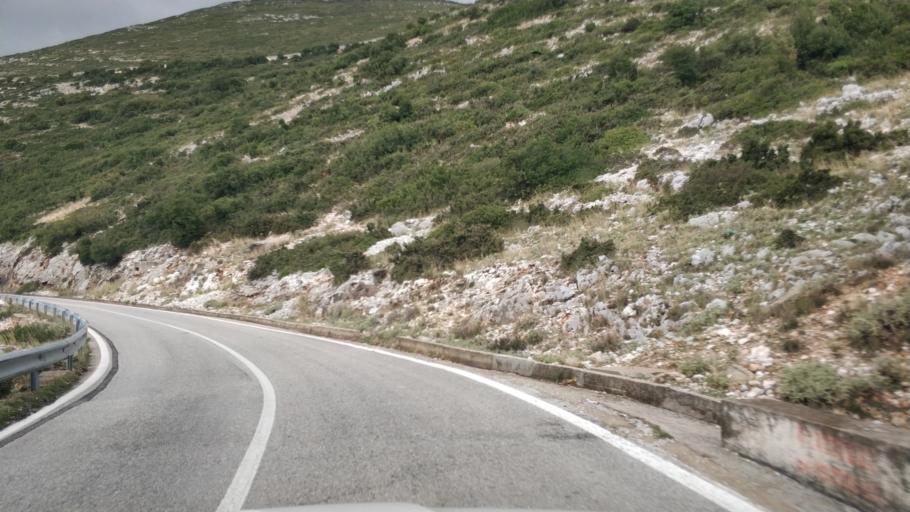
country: AL
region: Vlore
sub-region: Rrethi i Vlores
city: Vranisht
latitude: 40.1768
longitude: 19.6047
